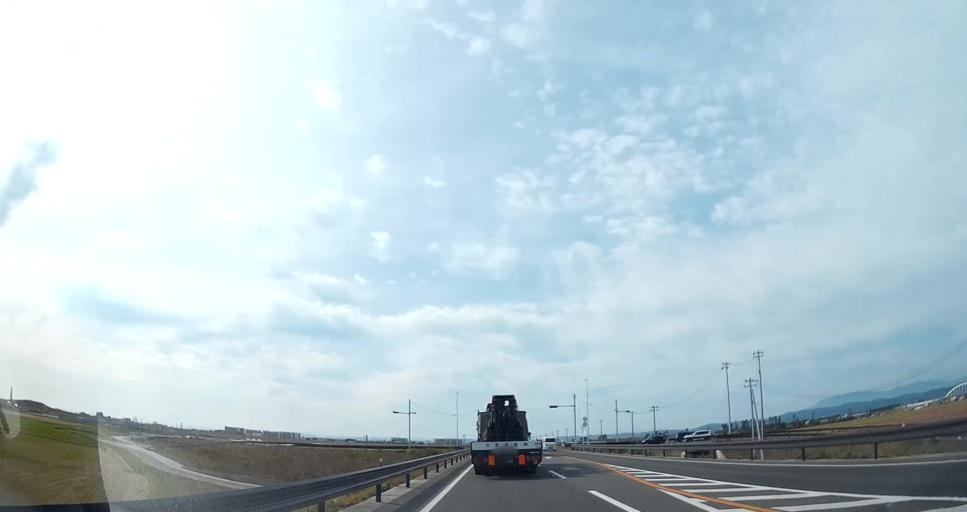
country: JP
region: Miyagi
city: Sendai
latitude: 38.1897
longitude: 140.9547
